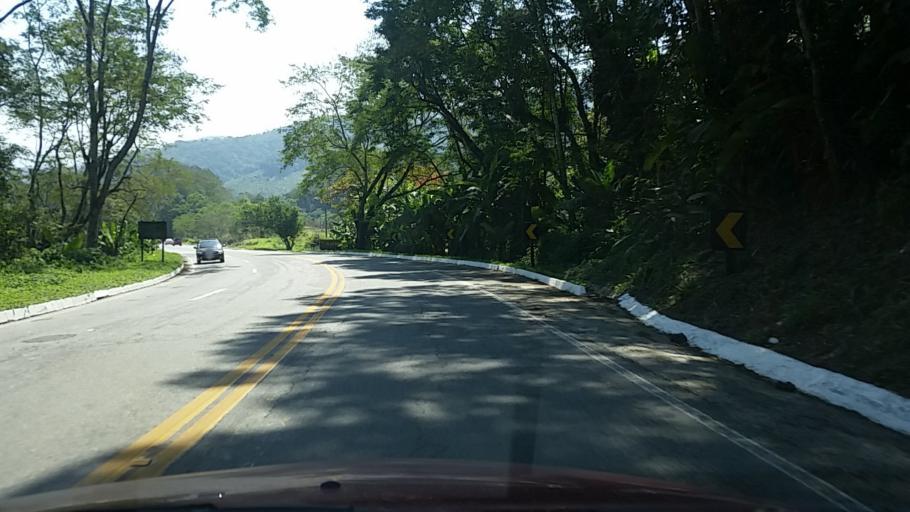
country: BR
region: Sao Paulo
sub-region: Miracatu
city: Miracatu
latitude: -24.3456
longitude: -47.4979
